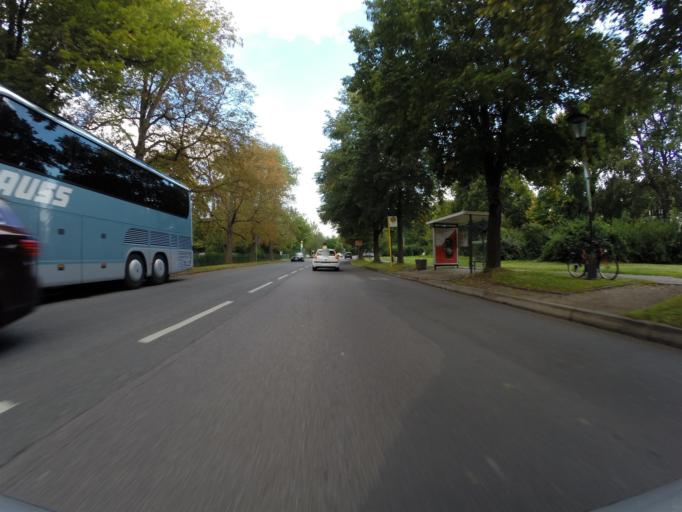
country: DE
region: Thuringia
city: Weimar
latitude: 50.9662
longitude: 11.3383
